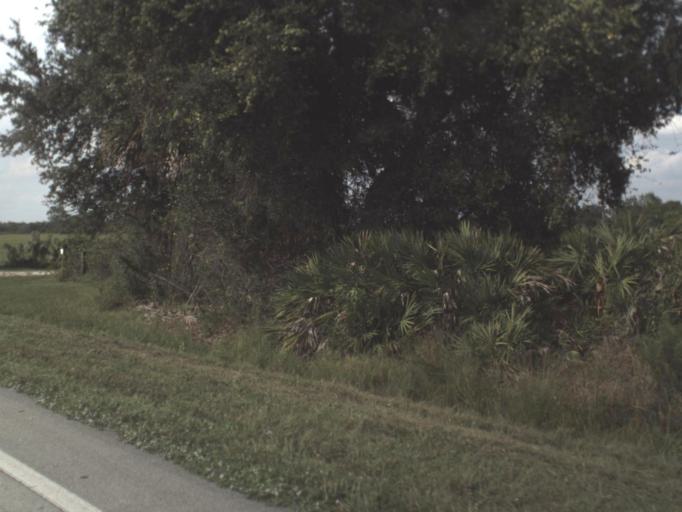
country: US
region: Florida
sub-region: Okeechobee County
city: Taylor Creek
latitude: 27.1787
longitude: -80.7070
